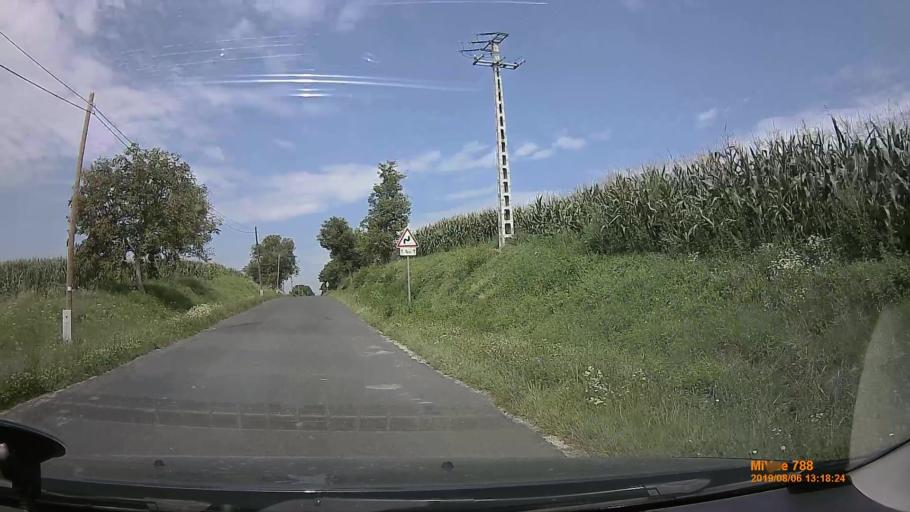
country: HU
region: Zala
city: Pacsa
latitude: 46.6329
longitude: 17.0611
